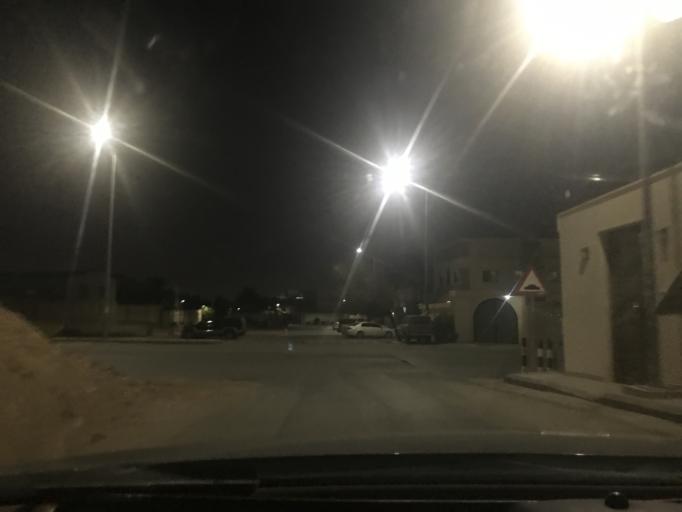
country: SA
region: Ar Riyad
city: Riyadh
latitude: 24.7408
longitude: 46.7623
